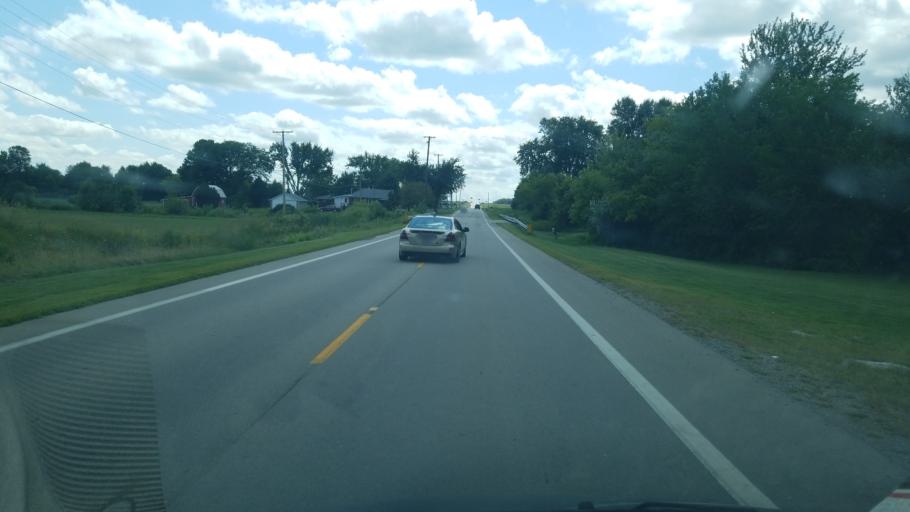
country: US
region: Ohio
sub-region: Henry County
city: Liberty Center
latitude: 41.4395
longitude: -84.0088
